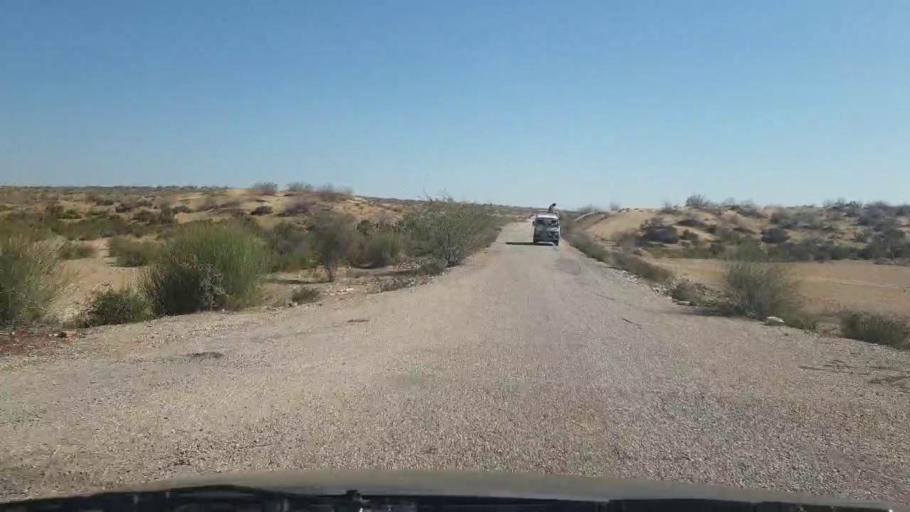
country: PK
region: Sindh
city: Bozdar
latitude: 27.0194
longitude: 68.7285
